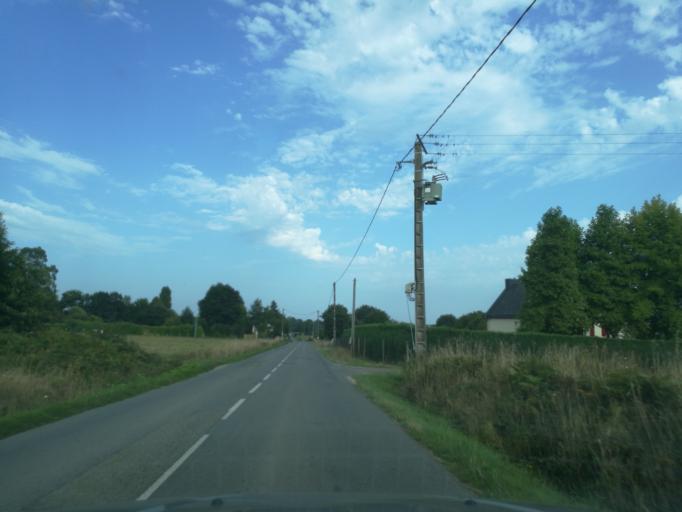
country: FR
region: Brittany
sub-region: Departement d'Ille-et-Vilaine
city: Montauban-de-Bretagne
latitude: 48.1996
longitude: -2.0105
